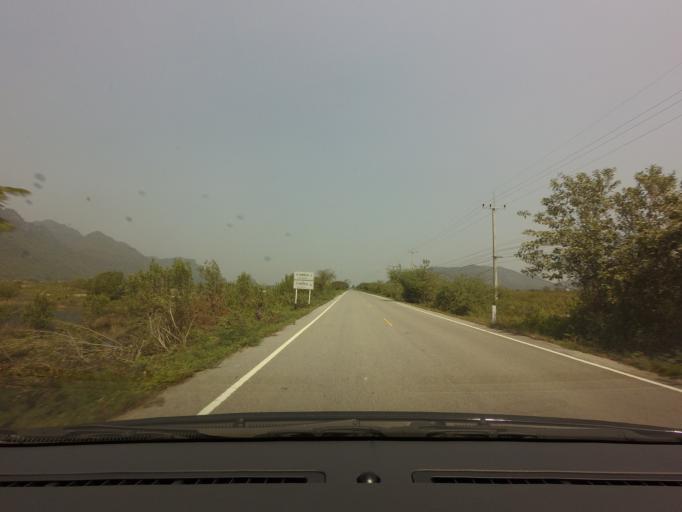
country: TH
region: Prachuap Khiri Khan
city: Sam Roi Yot
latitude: 12.1896
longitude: 99.9773
